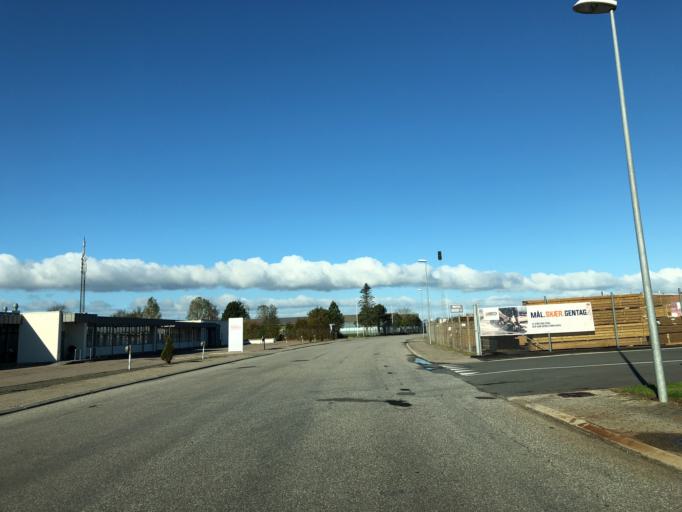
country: DK
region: Central Jutland
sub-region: Holstebro Kommune
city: Holstebro
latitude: 56.3787
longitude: 8.6180
